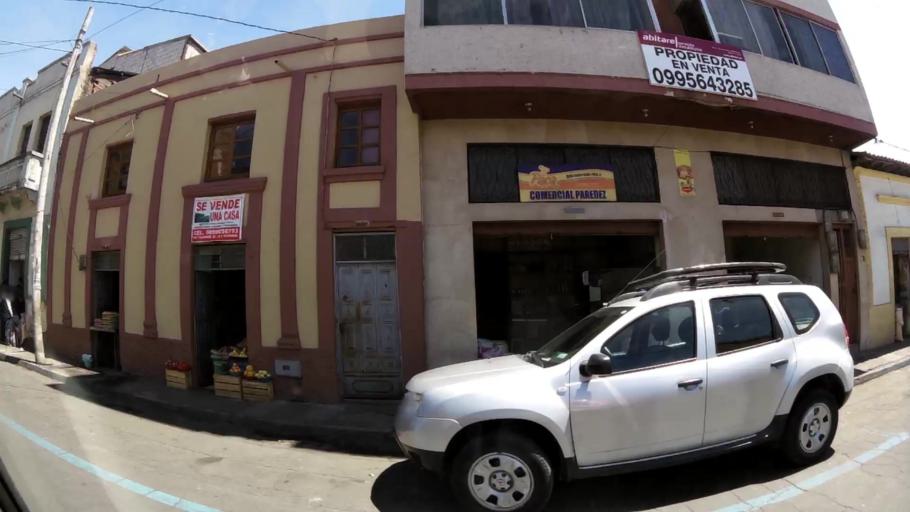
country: EC
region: Chimborazo
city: Riobamba
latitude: -1.6729
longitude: -78.6533
